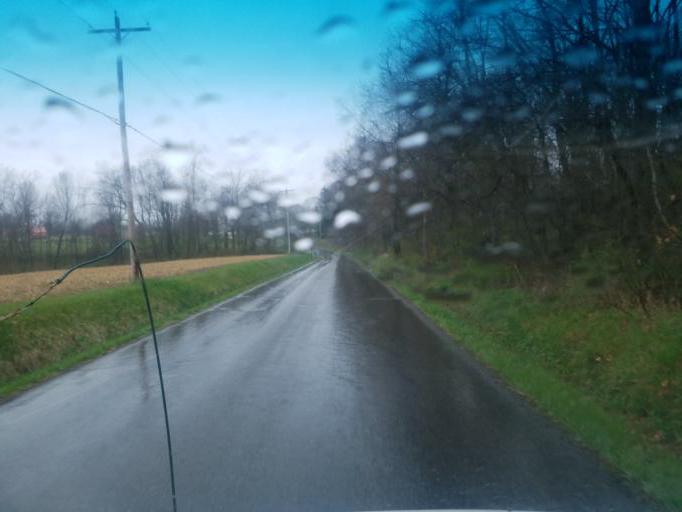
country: US
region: Ohio
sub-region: Wayne County
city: Wooster
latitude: 40.7326
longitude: -81.9293
